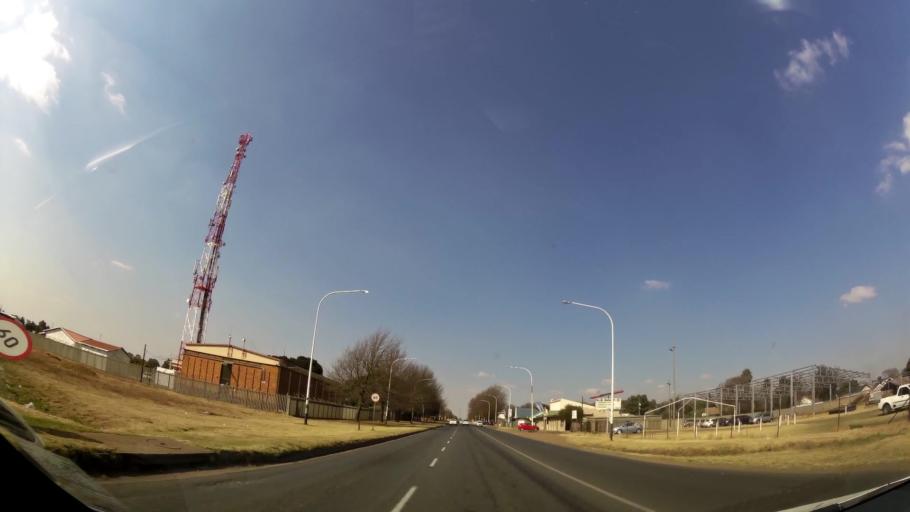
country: ZA
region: Gauteng
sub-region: Ekurhuleni Metropolitan Municipality
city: Boksburg
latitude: -26.1856
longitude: 28.2203
